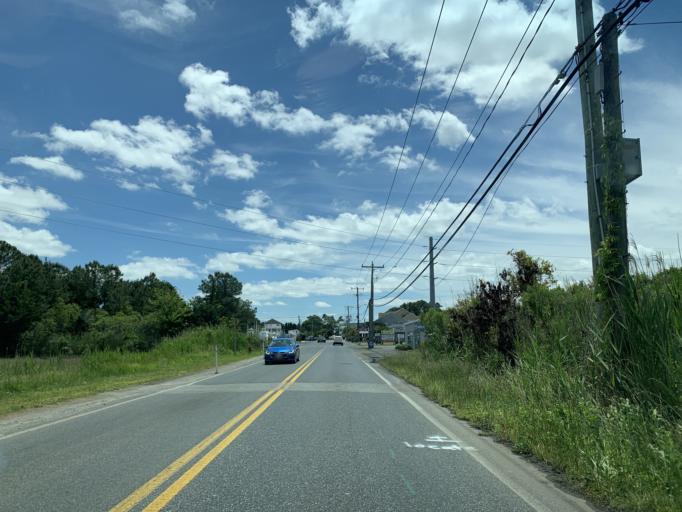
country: US
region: Maryland
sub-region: Worcester County
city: West Ocean City
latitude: 38.3289
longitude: -75.1074
